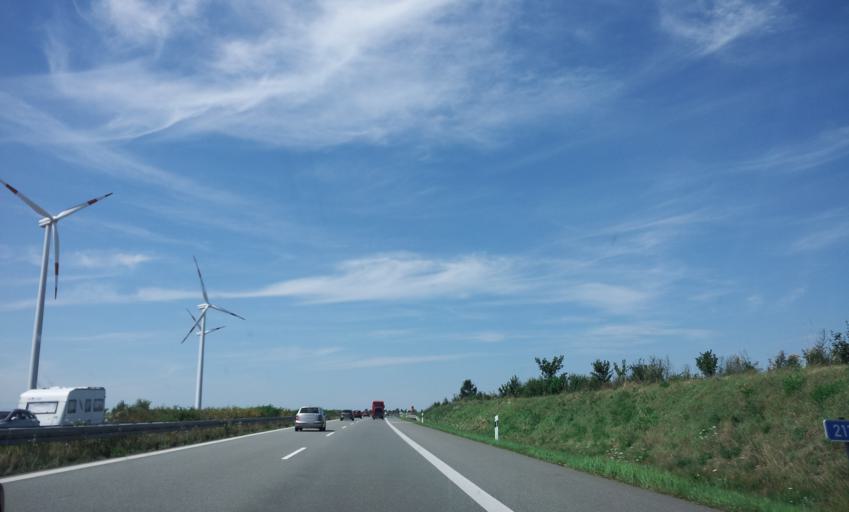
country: DE
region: Mecklenburg-Vorpommern
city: Gormin
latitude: 53.9967
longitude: 13.3202
